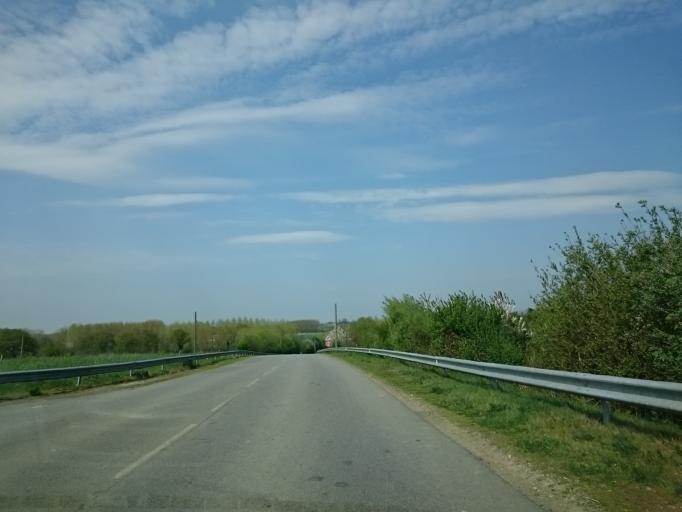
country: FR
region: Brittany
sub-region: Departement d'Ille-et-Vilaine
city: Saint-Armel
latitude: 48.0241
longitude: -1.6002
